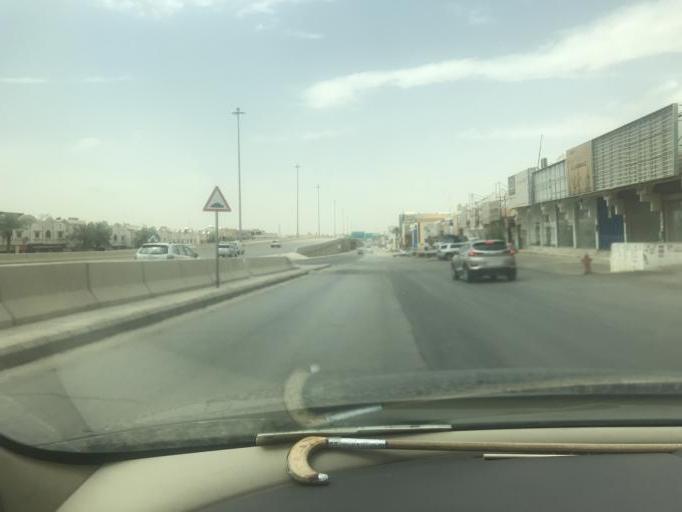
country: SA
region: Ar Riyad
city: Riyadh
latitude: 24.7869
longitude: 46.7038
